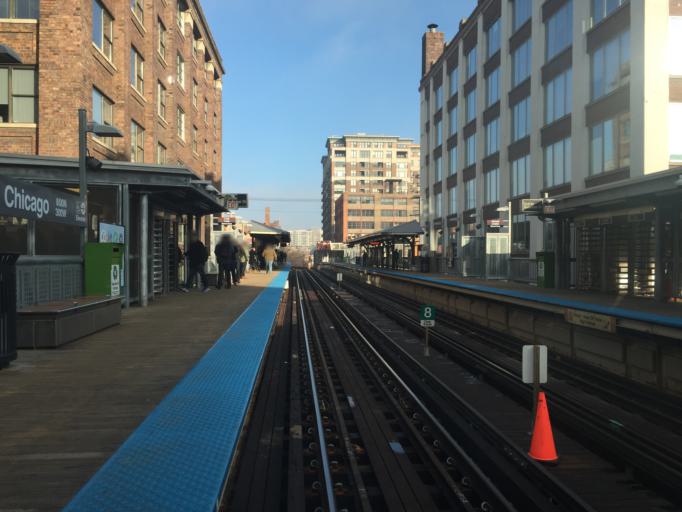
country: US
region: Illinois
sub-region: Cook County
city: Chicago
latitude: 41.8956
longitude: -87.6357
